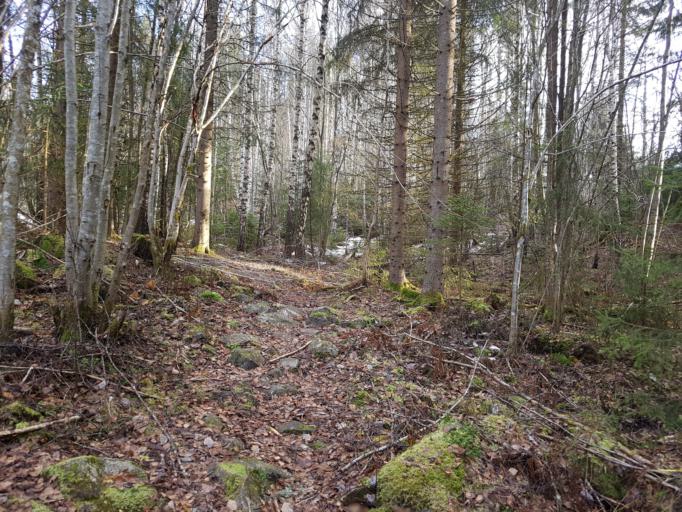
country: NO
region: Oppland
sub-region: Lillehammer
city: Lillehammer
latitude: 61.1091
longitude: 10.4828
